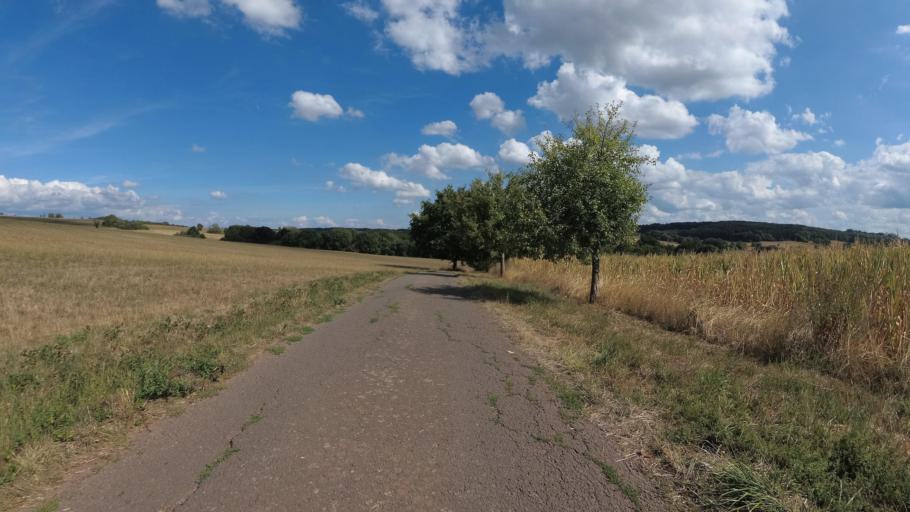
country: DE
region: Saarland
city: Mainzweiler
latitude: 49.4089
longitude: 7.0981
